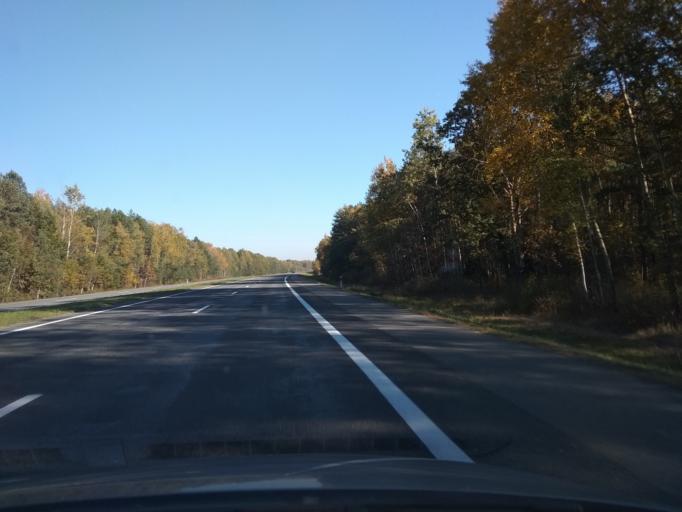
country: BY
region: Brest
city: Antopal'
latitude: 52.3507
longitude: 24.6761
